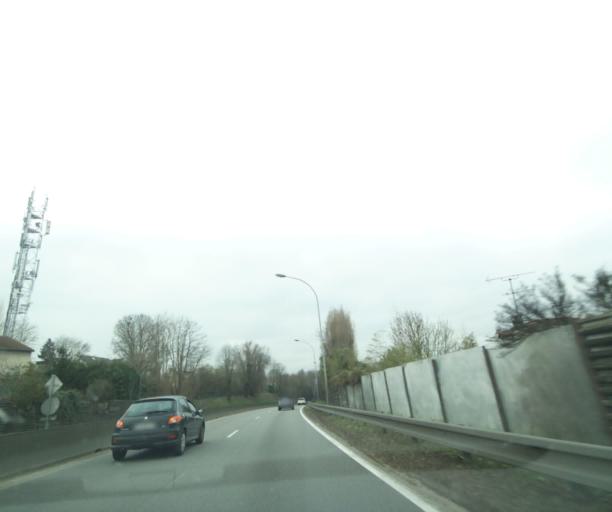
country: FR
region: Ile-de-France
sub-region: Departement des Yvelines
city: Saint-Germain-en-Laye
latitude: 48.8892
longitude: 2.0852
